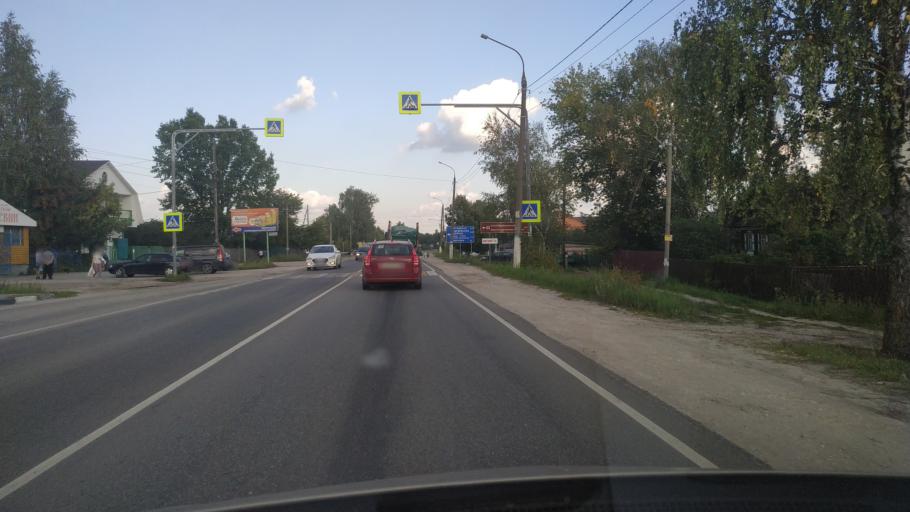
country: RU
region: Moskovskaya
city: Shatura
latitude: 55.5772
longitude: 39.4932
